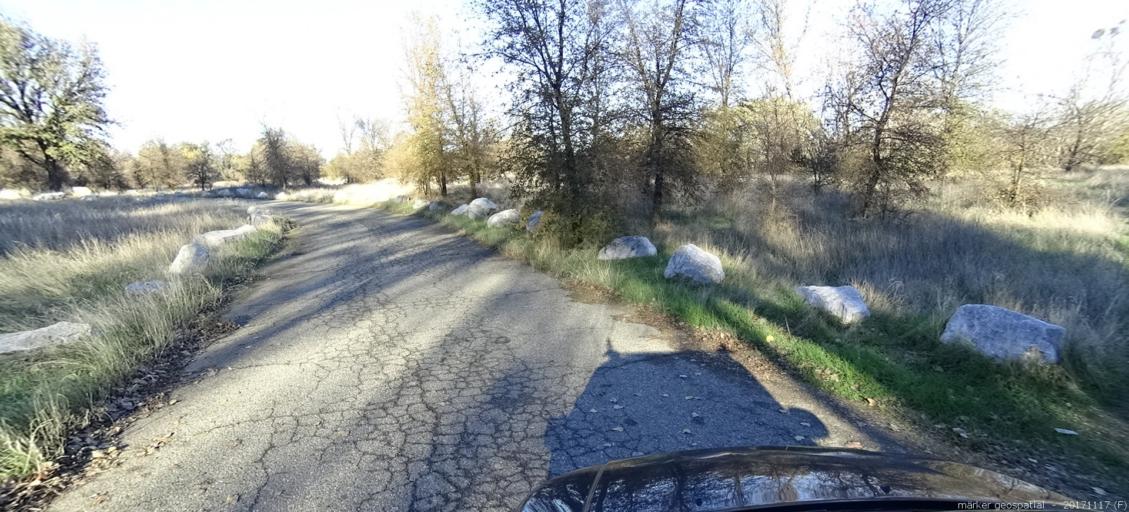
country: US
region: California
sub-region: Shasta County
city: Cottonwood
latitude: 40.3903
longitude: -122.1971
